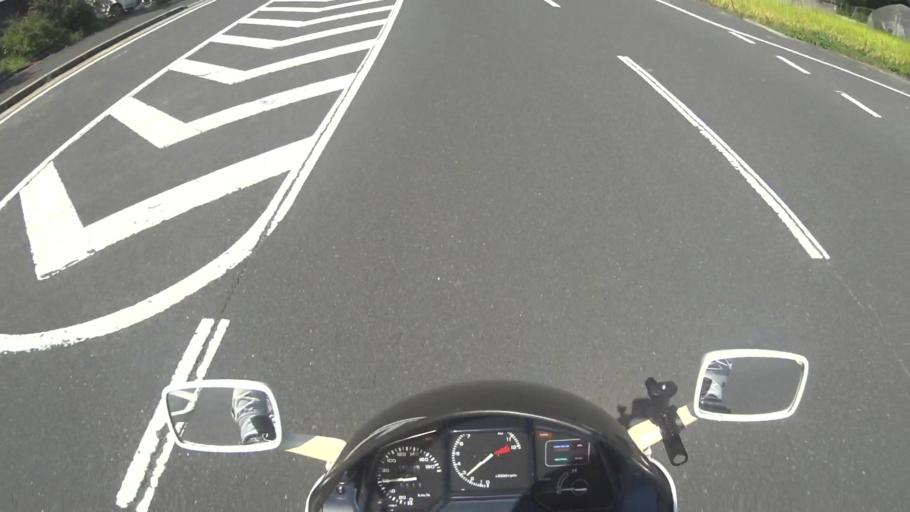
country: JP
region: Kyoto
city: Miyazu
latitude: 35.7315
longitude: 135.2581
